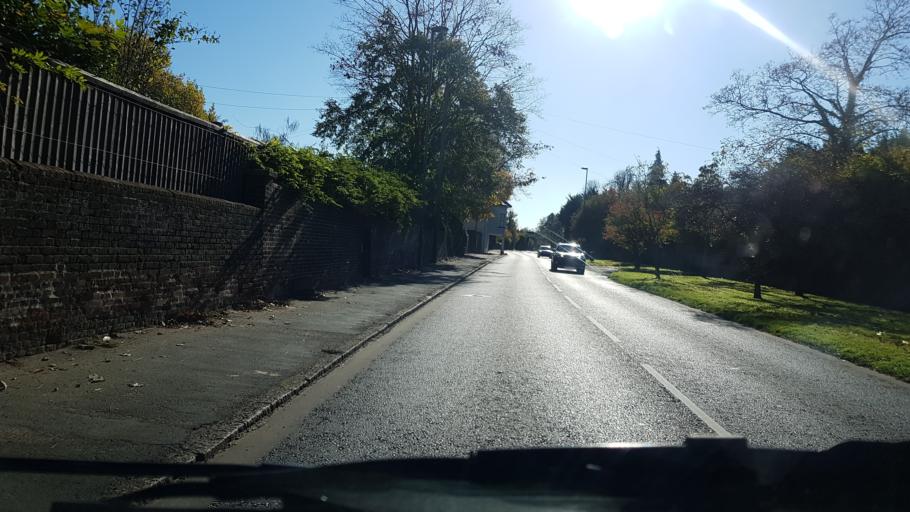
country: GB
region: England
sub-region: Surrey
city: Shalford
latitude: 51.2184
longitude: -0.5685
